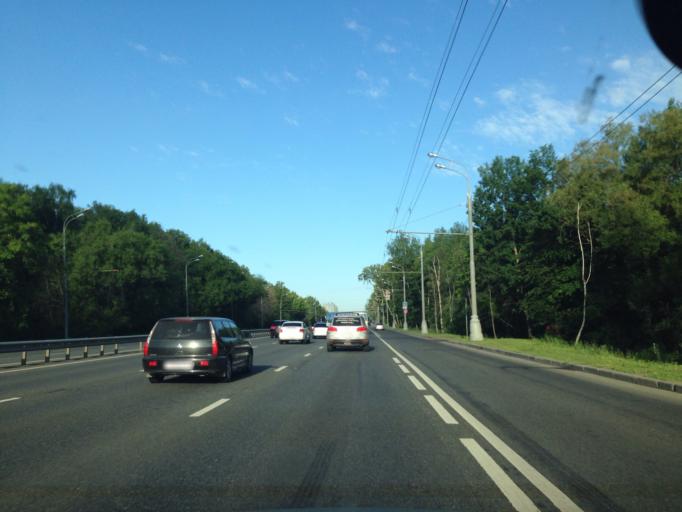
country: RU
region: Moskovskaya
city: Izmaylovo
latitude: 55.7695
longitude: 37.8085
